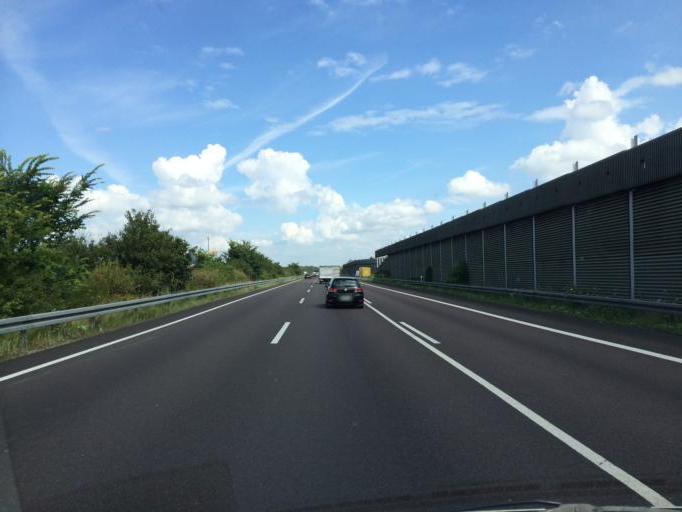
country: DE
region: Lower Saxony
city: Konigslutter am Elm
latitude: 52.3110
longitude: 10.8161
